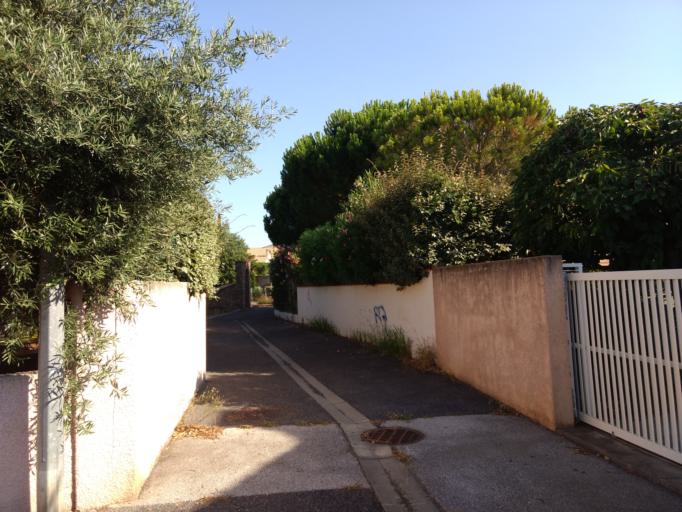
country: FR
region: Languedoc-Roussillon
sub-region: Departement des Pyrenees-Orientales
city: Cabestany
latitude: 42.6933
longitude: 2.9369
